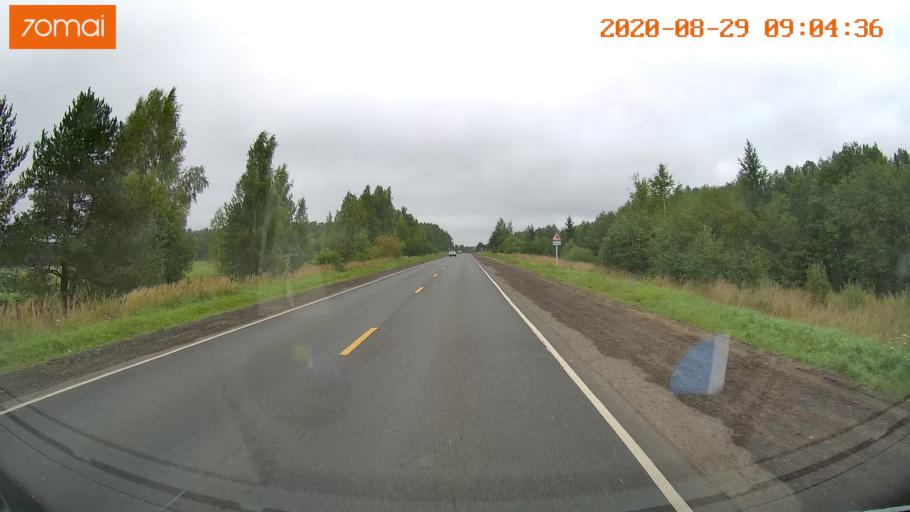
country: RU
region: Ivanovo
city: Navoloki
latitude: 57.3498
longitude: 41.9861
